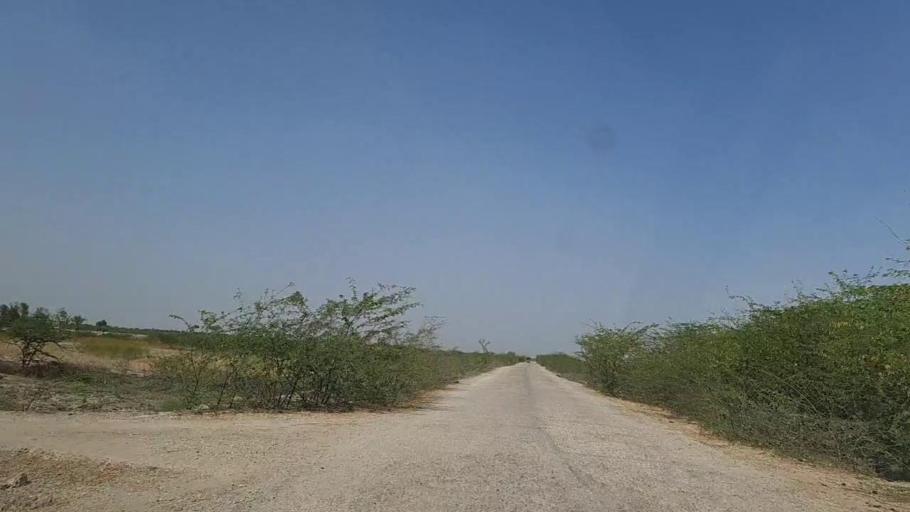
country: PK
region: Sindh
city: Naukot
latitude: 24.6389
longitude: 69.2879
